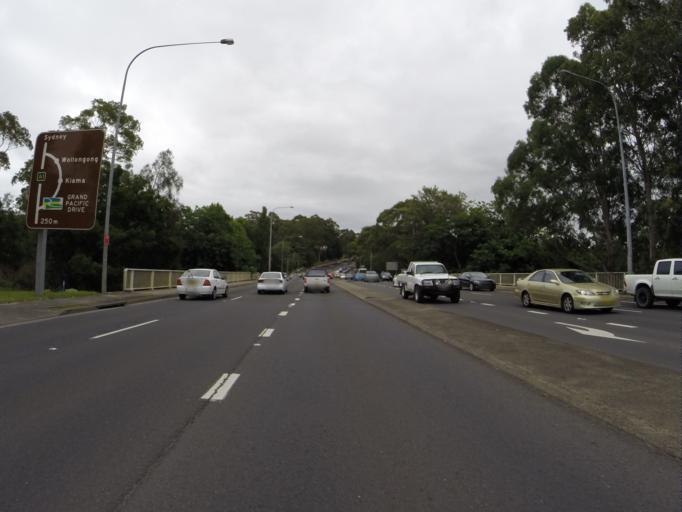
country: AU
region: New South Wales
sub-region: Shoalhaven Shire
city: Bomaderry
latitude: -34.8615
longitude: 150.6007
